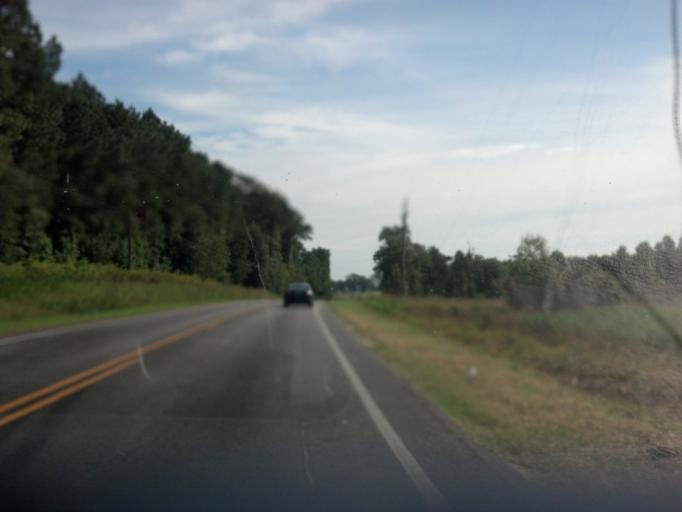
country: US
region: North Carolina
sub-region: Greene County
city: Snow Hill
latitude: 35.4805
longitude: -77.6497
